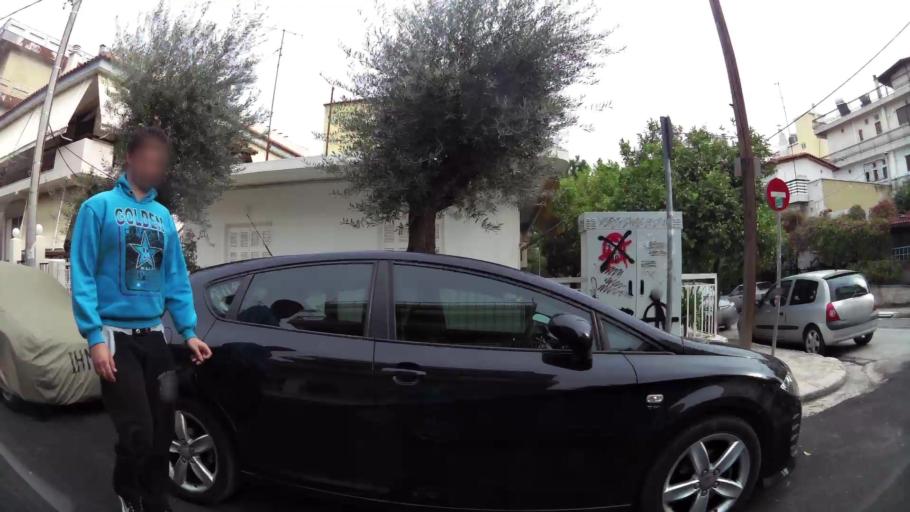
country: GR
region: Attica
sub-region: Nomarchia Athinas
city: Agios Dimitrios
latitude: 37.9223
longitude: 23.7371
